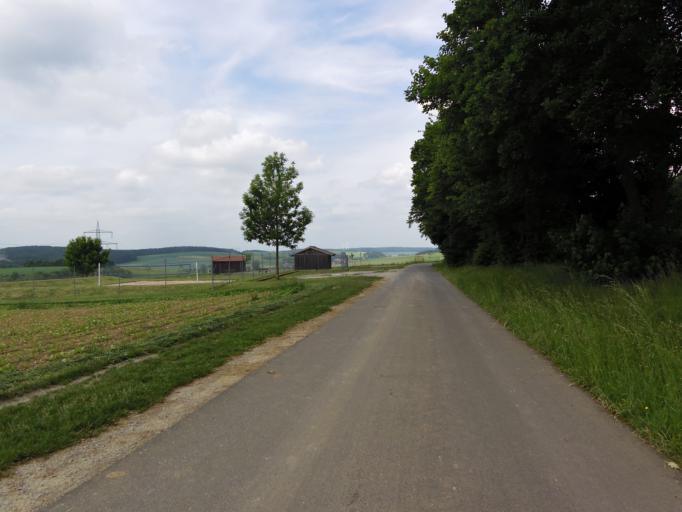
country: DE
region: Bavaria
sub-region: Regierungsbezirk Unterfranken
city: Waldbrunn
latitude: 49.7675
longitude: 9.7937
